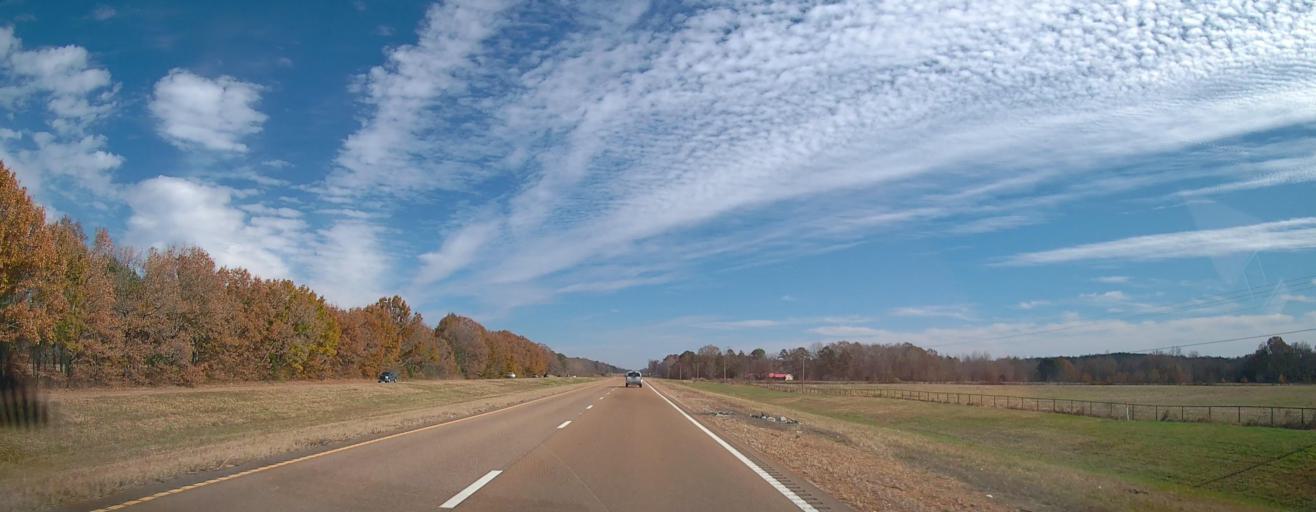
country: US
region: Mississippi
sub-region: Benton County
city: Ashland
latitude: 34.9460
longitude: -89.1373
